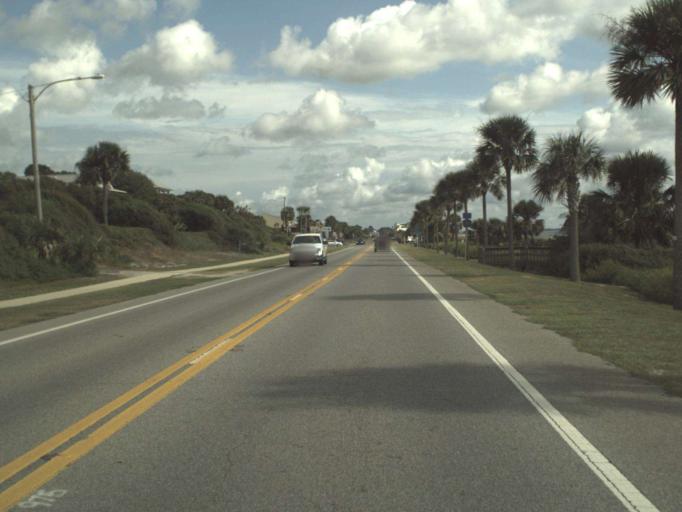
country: US
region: Florida
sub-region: Bay County
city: Mexico Beach
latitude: 29.9269
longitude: -85.3904
